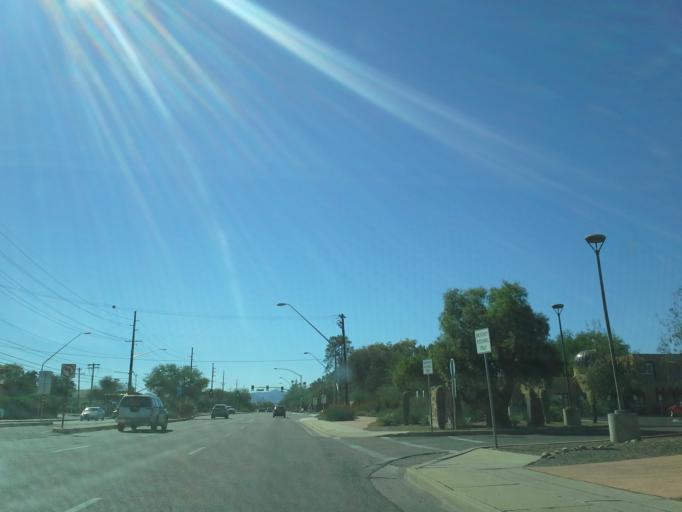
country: US
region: Arizona
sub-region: Pima County
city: Tucson
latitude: 32.2508
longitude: -110.8782
